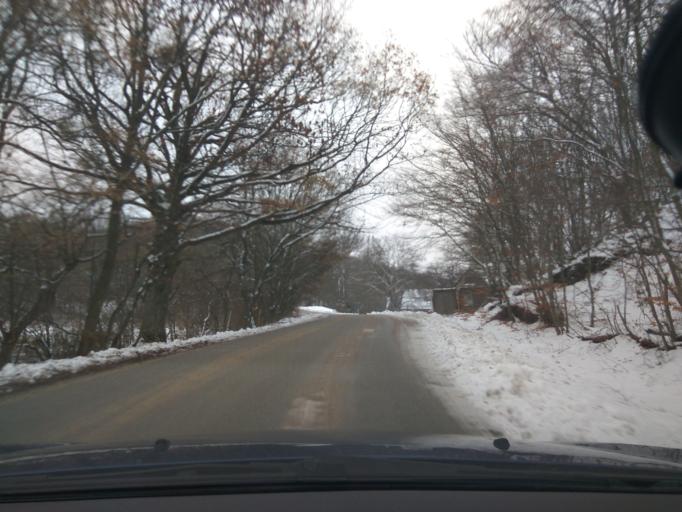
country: SK
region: Nitriansky
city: Stara Tura
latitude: 48.8230
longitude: 17.7036
